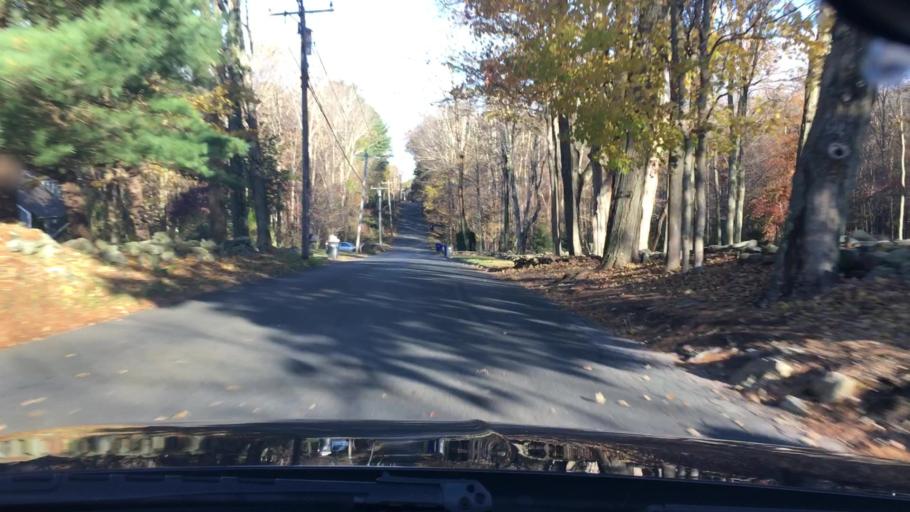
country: US
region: Connecticut
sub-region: Tolland County
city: Crystal Lake
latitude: 41.9533
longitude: -72.4016
